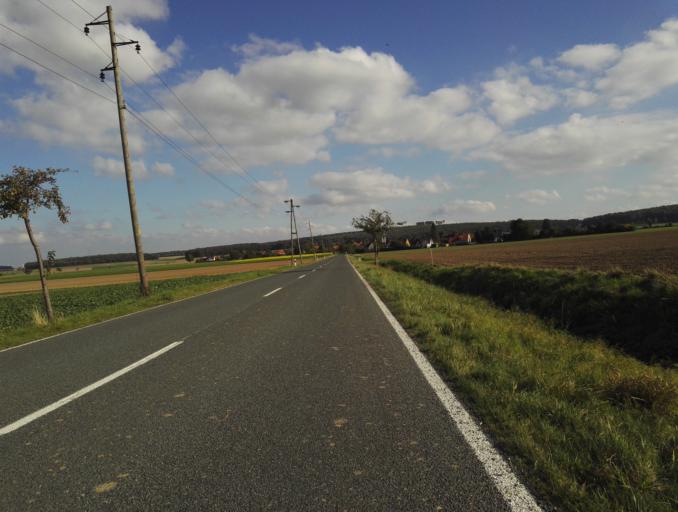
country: DE
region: Lower Saxony
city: Schellerten
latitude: 52.1483
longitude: 10.1183
